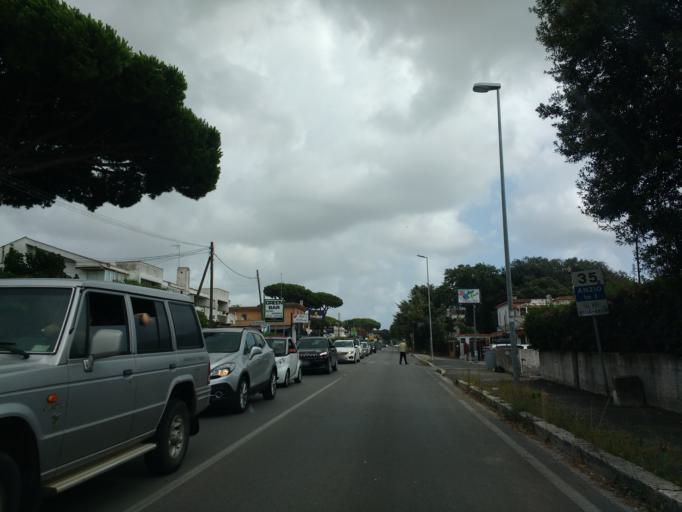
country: IT
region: Latium
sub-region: Citta metropolitana di Roma Capitale
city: Anzio
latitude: 41.4854
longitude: 12.6007
